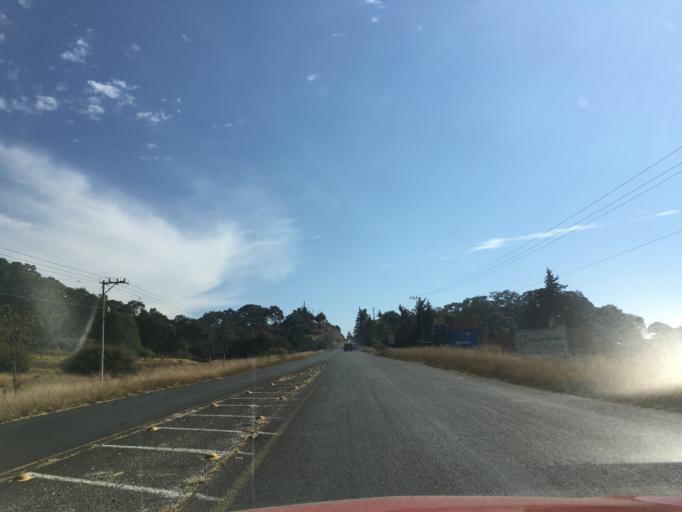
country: MX
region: Michoacan
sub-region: Hidalgo
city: Rincon de Cedenos (Rincon de Dolores)
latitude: 19.6992
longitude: -100.5871
